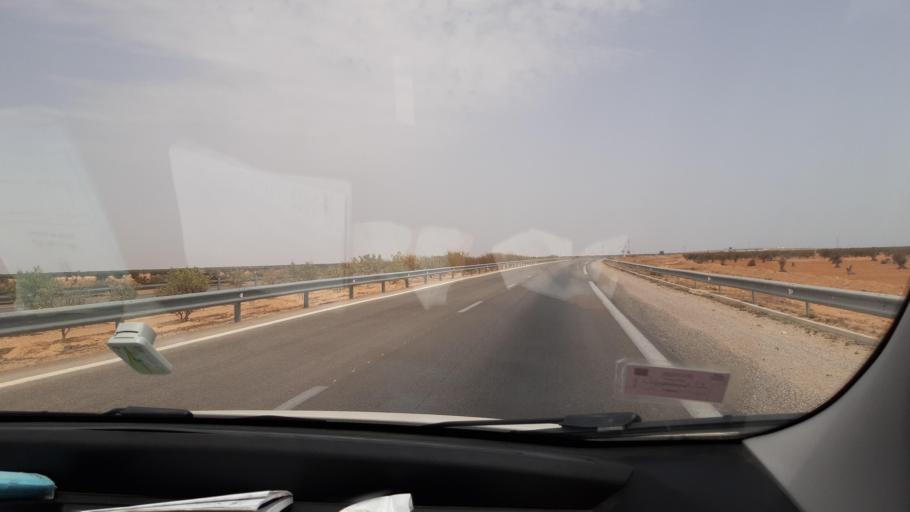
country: TN
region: Safaqis
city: Bi'r `Ali Bin Khalifah
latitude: 34.5910
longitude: 10.4189
